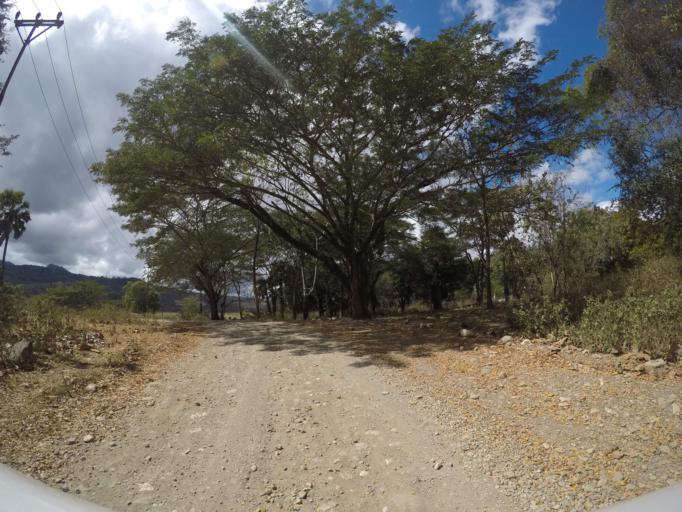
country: TL
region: Lautem
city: Lospalos
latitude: -8.4883
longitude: 126.8196
